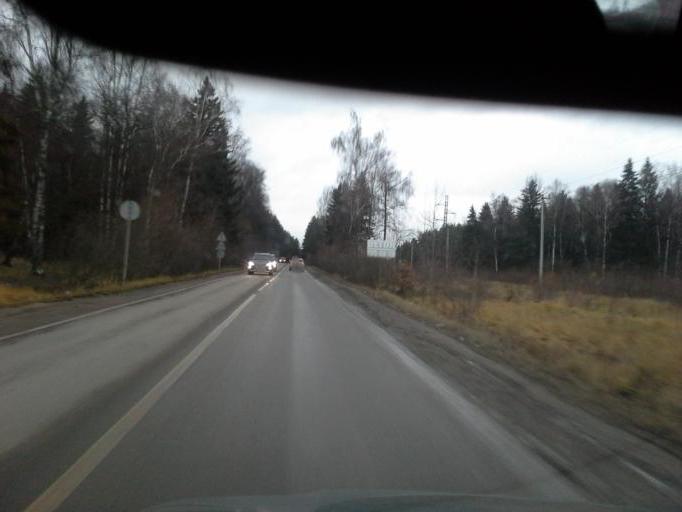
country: RU
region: Moskovskaya
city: Kokoshkino
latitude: 55.6055
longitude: 37.1642
